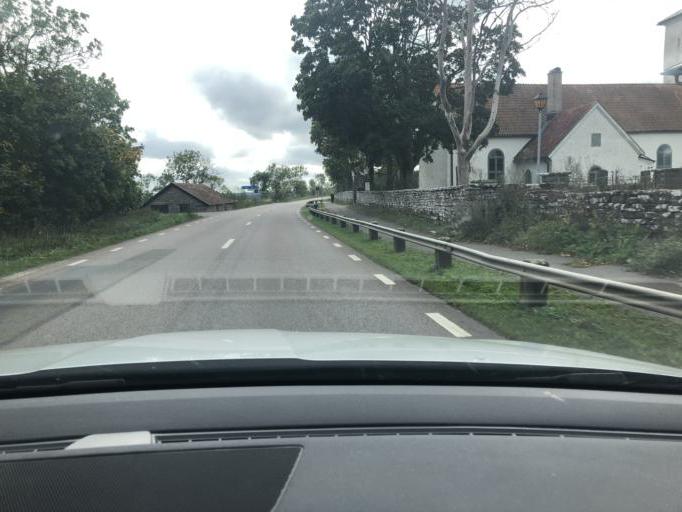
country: SE
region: Kalmar
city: Faerjestaden
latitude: 56.5777
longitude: 16.4607
